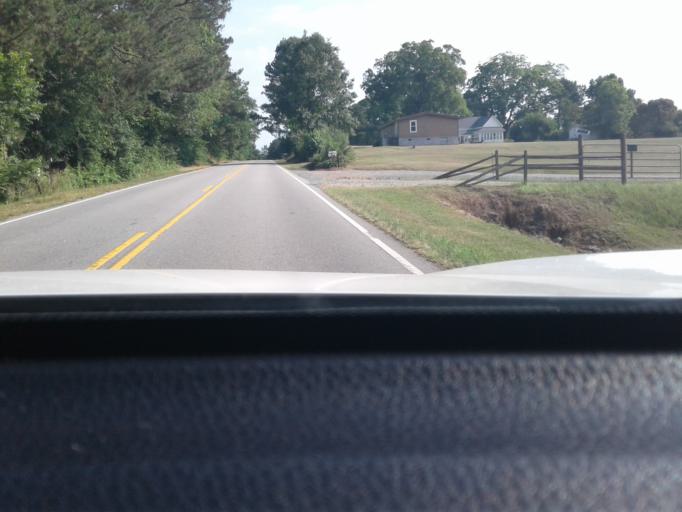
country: US
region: North Carolina
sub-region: Johnston County
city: Benson
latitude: 35.4091
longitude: -78.5404
